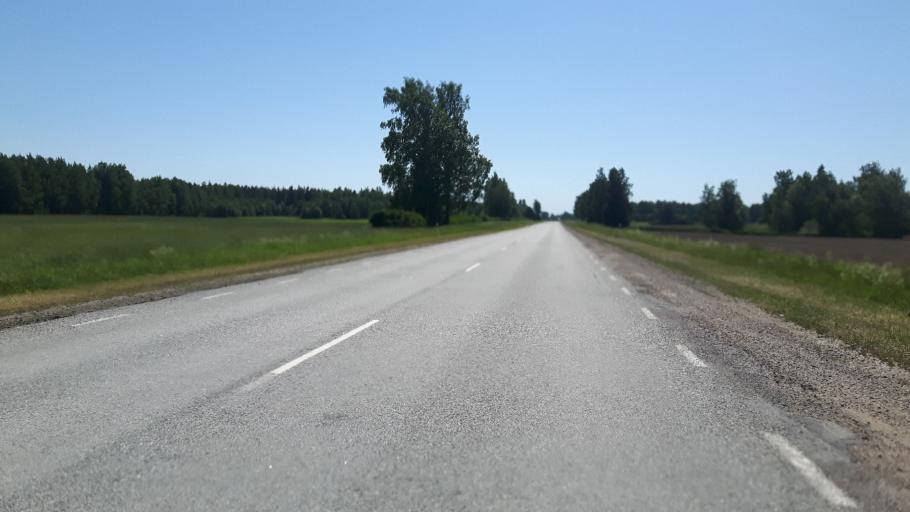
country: EE
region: Paernumaa
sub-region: Tootsi vald
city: Tootsi
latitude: 58.4609
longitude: 24.7814
